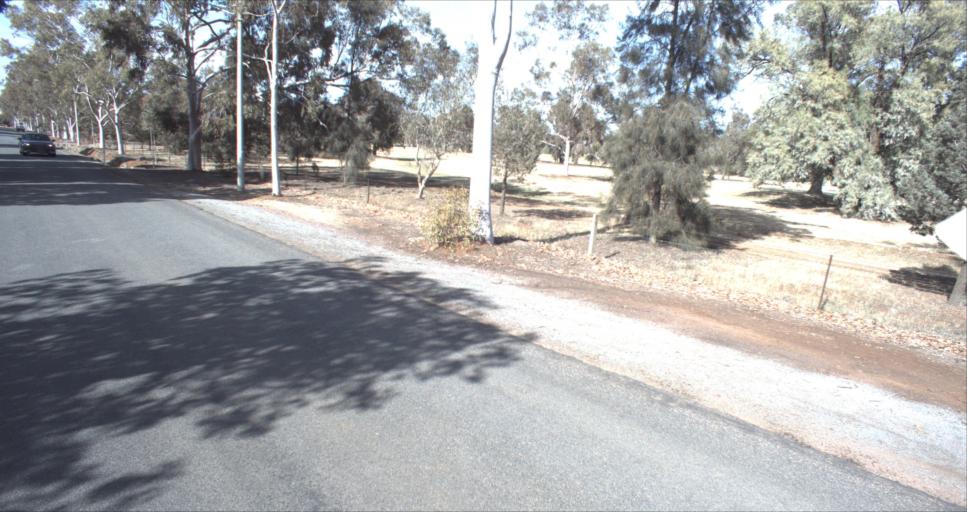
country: AU
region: New South Wales
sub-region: Leeton
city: Leeton
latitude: -34.5614
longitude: 146.4099
